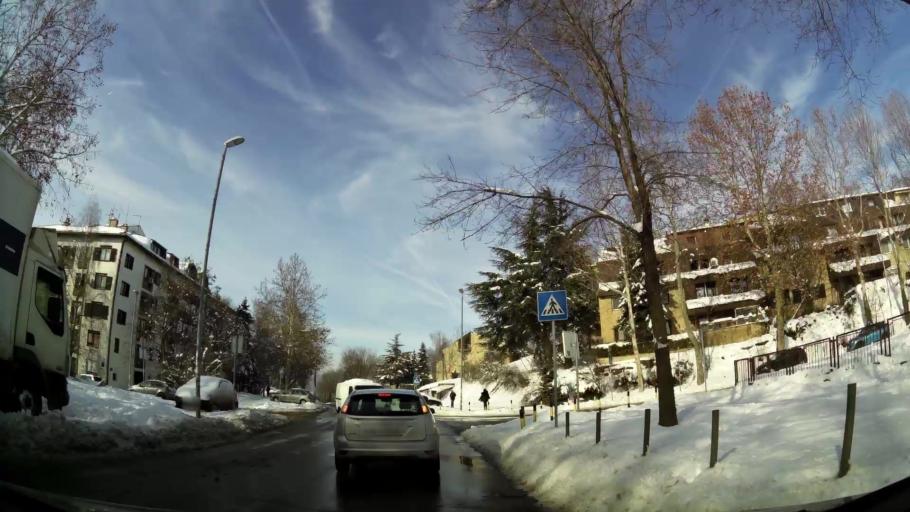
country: RS
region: Central Serbia
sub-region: Belgrade
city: Zvezdara
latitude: 44.7928
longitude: 20.5395
